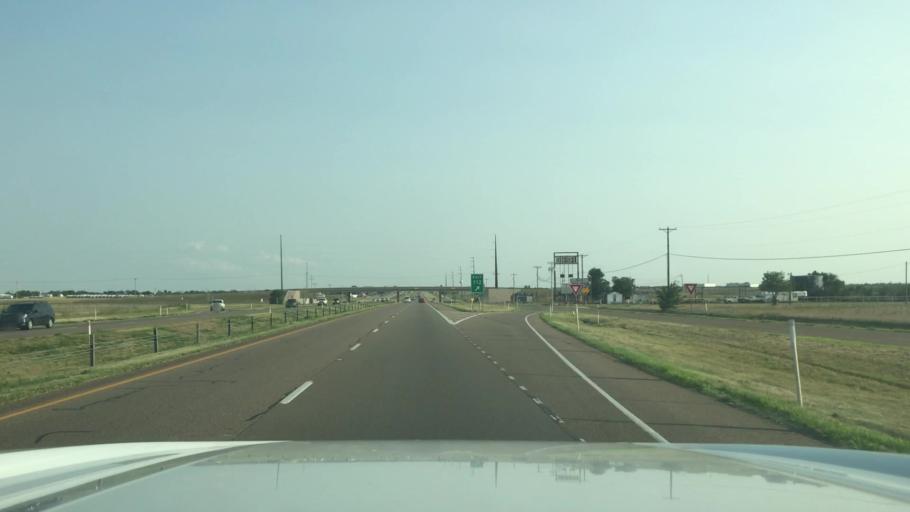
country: US
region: Texas
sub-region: Randall County
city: Canyon
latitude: 35.0616
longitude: -101.9193
